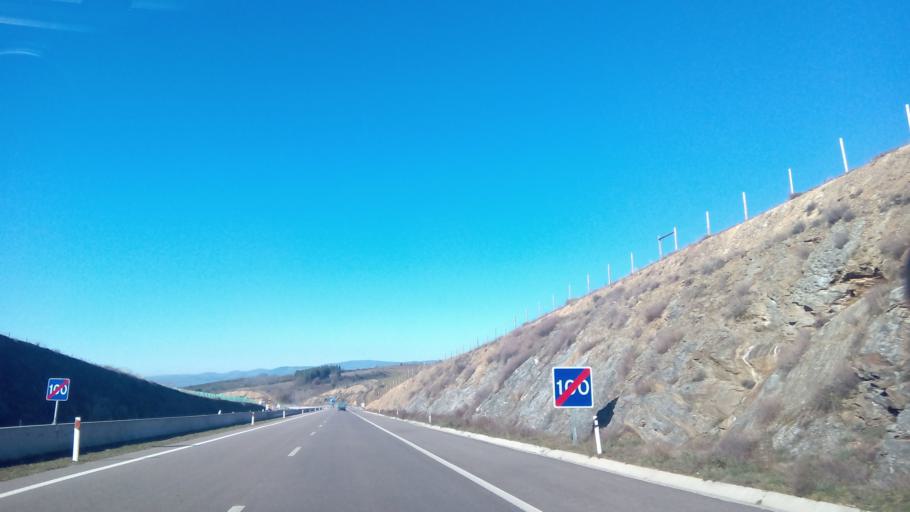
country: ES
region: Castille and Leon
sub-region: Provincia de Zamora
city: Trabazos
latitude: 41.7489
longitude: -6.6277
